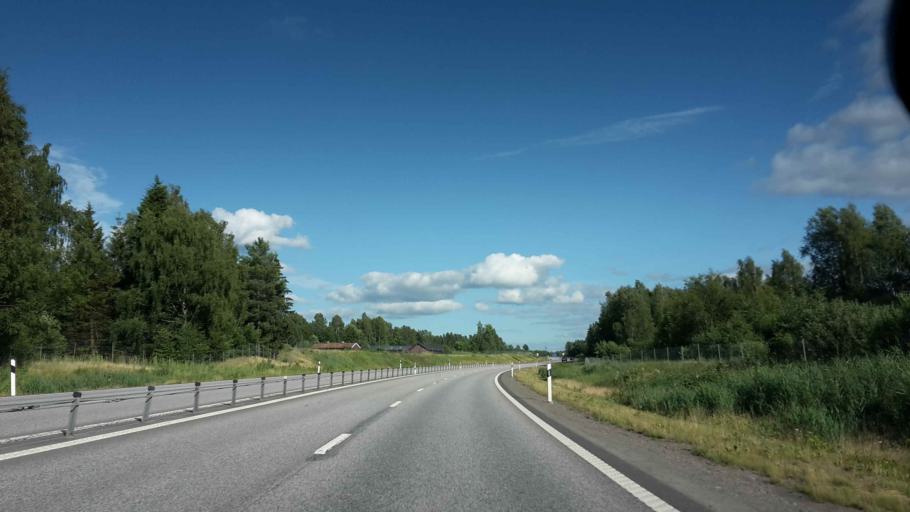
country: SE
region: OEstergoetland
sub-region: Norrkopings Kommun
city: Svartinge
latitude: 58.6439
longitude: 16.0814
